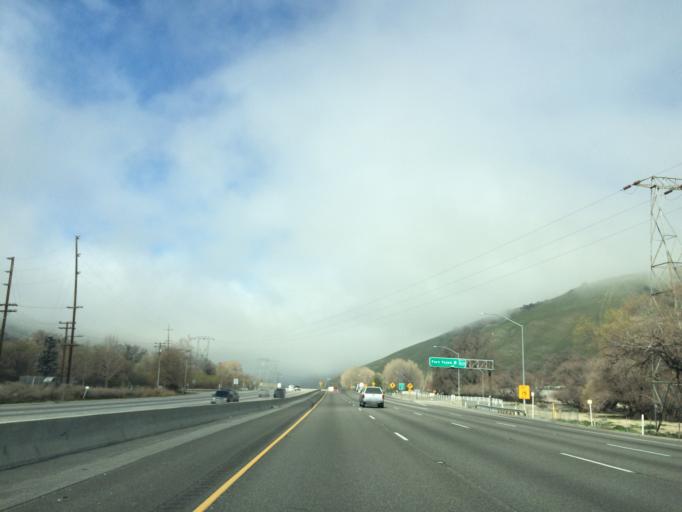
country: US
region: California
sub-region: Kern County
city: Lebec
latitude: 34.8726
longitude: -118.8899
